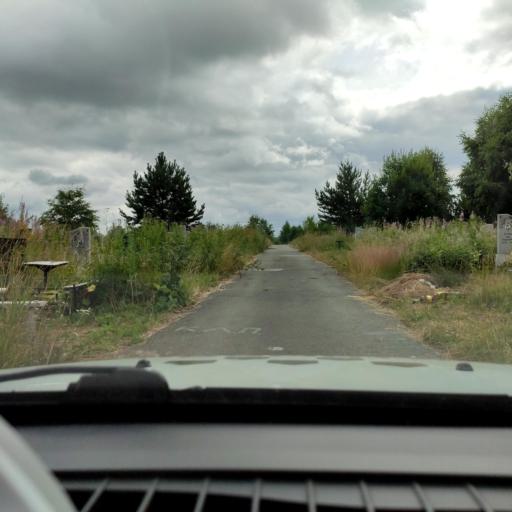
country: RU
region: Perm
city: Kondratovo
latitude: 58.0664
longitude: 56.1490
